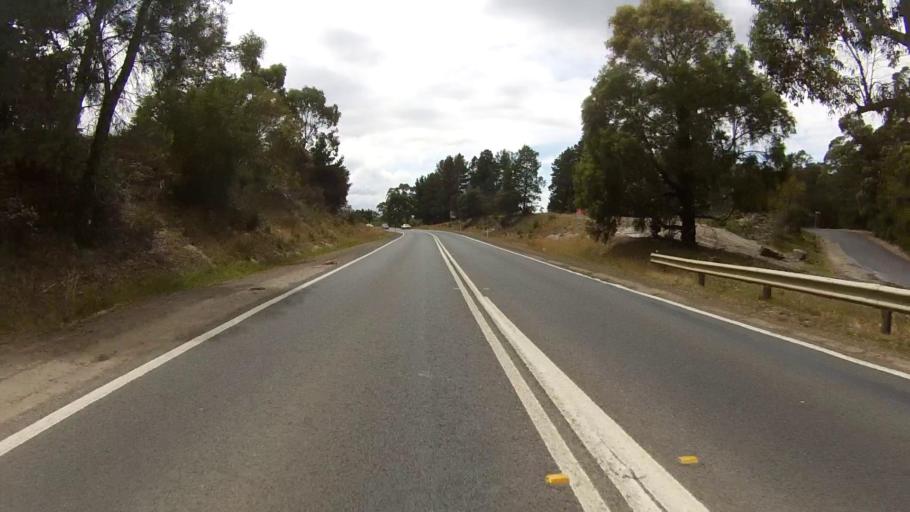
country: AU
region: Tasmania
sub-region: Kingborough
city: Margate
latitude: -43.0429
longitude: 147.2664
